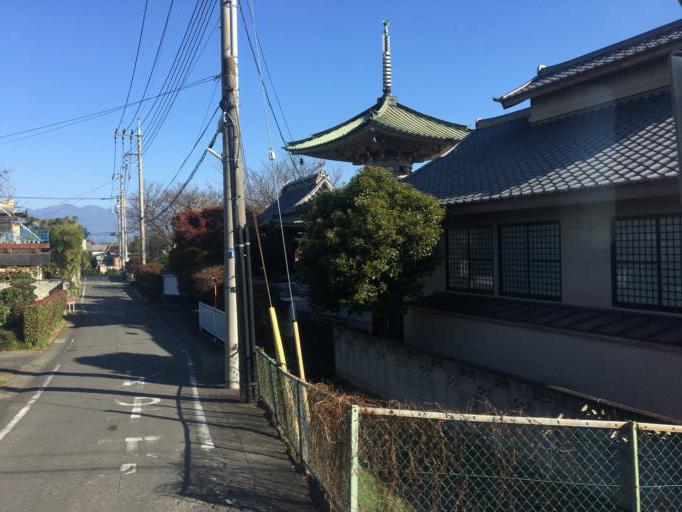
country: JP
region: Gunma
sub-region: Sawa-gun
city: Tamamura
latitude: 36.3556
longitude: 139.1365
